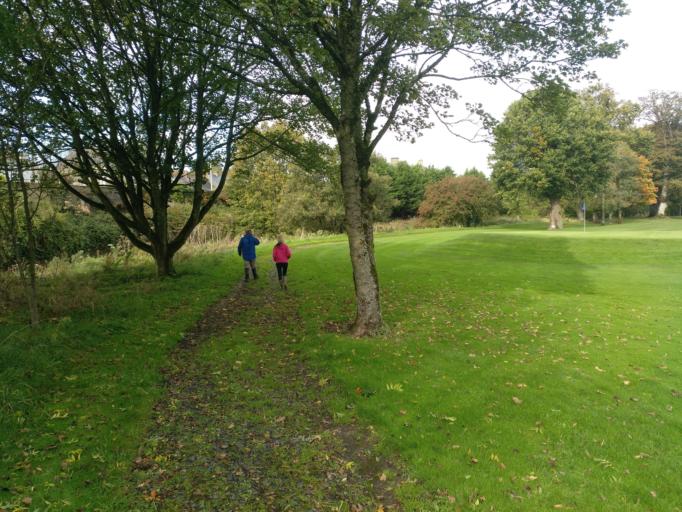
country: IE
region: Leinster
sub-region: Kilkenny
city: Castlecomer
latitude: 52.8006
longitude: -7.2093
